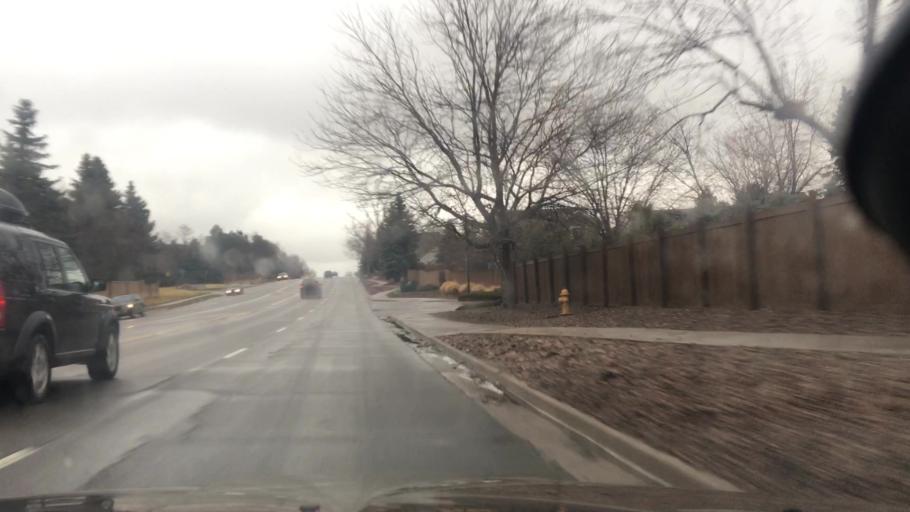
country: US
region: Colorado
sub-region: Arapahoe County
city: Castlewood
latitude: 39.5760
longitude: -104.9229
